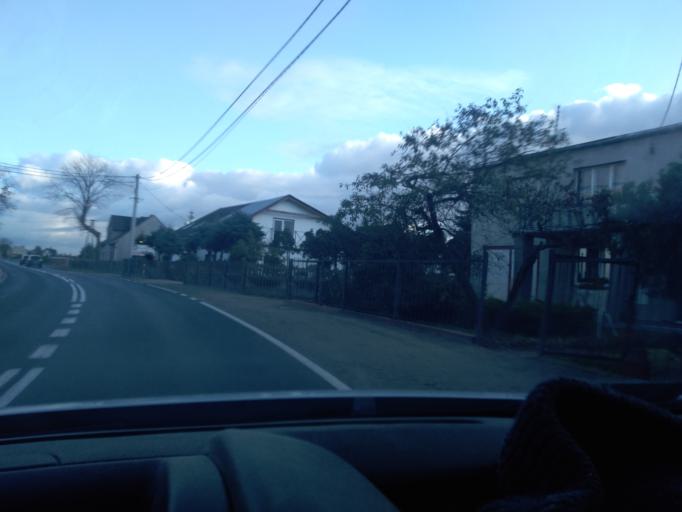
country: PL
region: Greater Poland Voivodeship
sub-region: Powiat poznanski
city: Murowana Goslina
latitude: 52.6362
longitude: 16.9471
